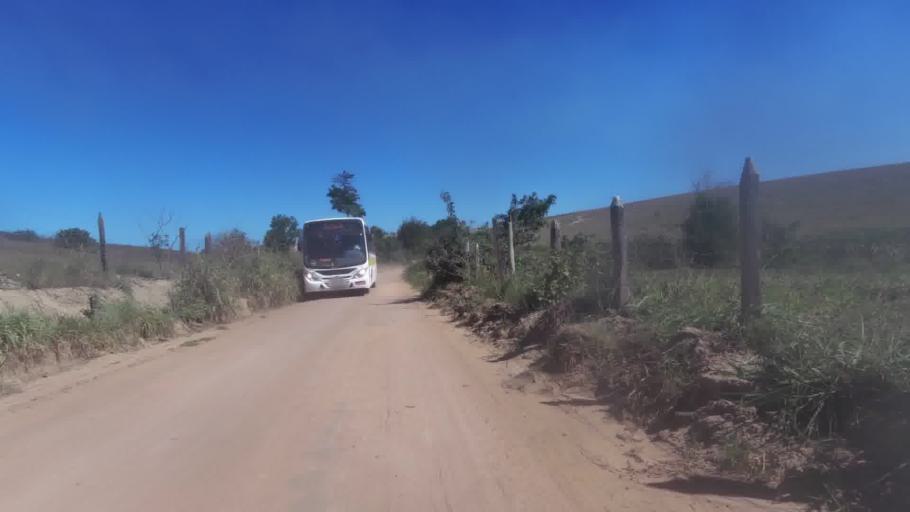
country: BR
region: Espirito Santo
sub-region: Marataizes
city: Marataizes
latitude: -21.1594
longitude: -40.9813
